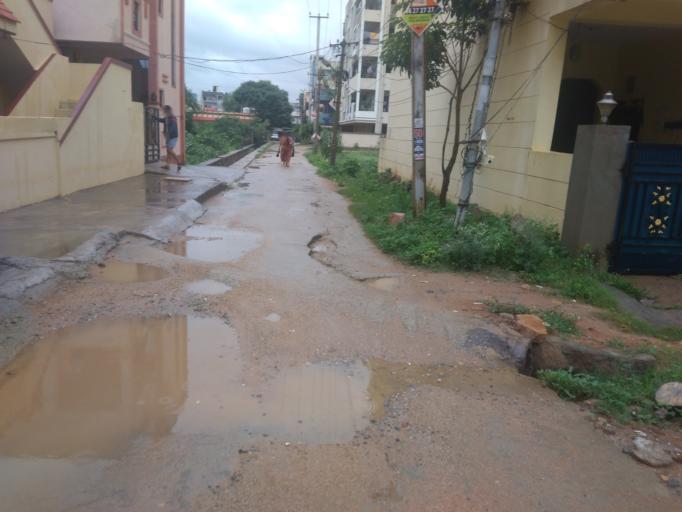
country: IN
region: Telangana
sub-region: Rangareddi
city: Secunderabad
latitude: 17.5120
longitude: 78.5088
